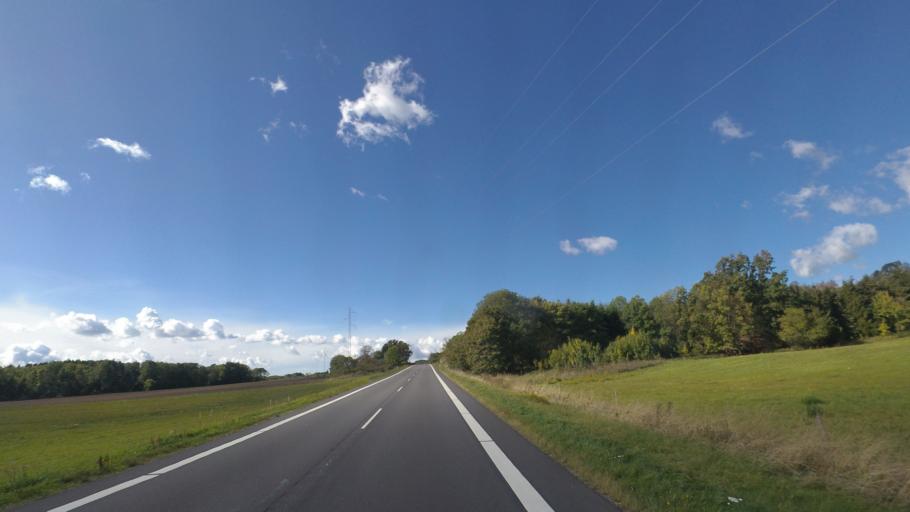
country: DK
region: Capital Region
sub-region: Bornholm Kommune
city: Nexo
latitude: 55.0616
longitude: 15.0388
